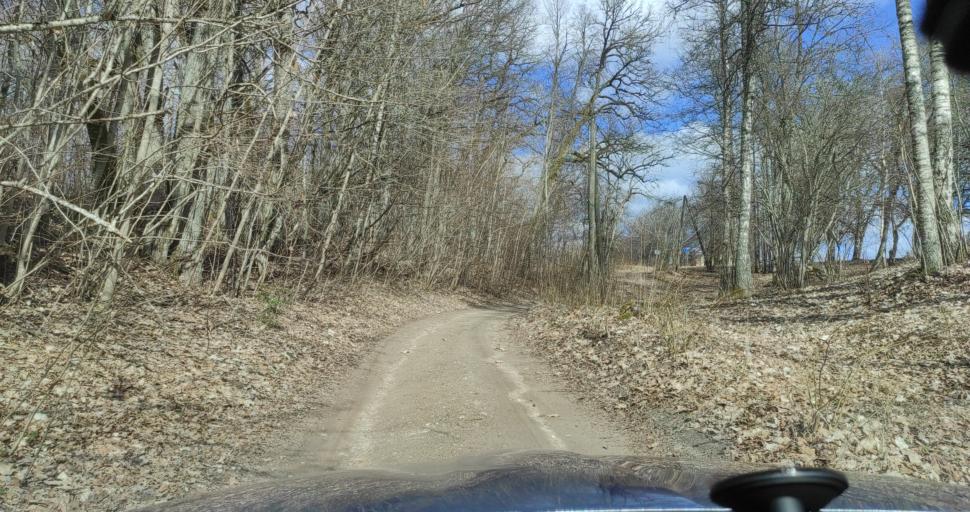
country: LV
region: Kuldigas Rajons
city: Kuldiga
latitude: 56.9599
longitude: 21.9195
